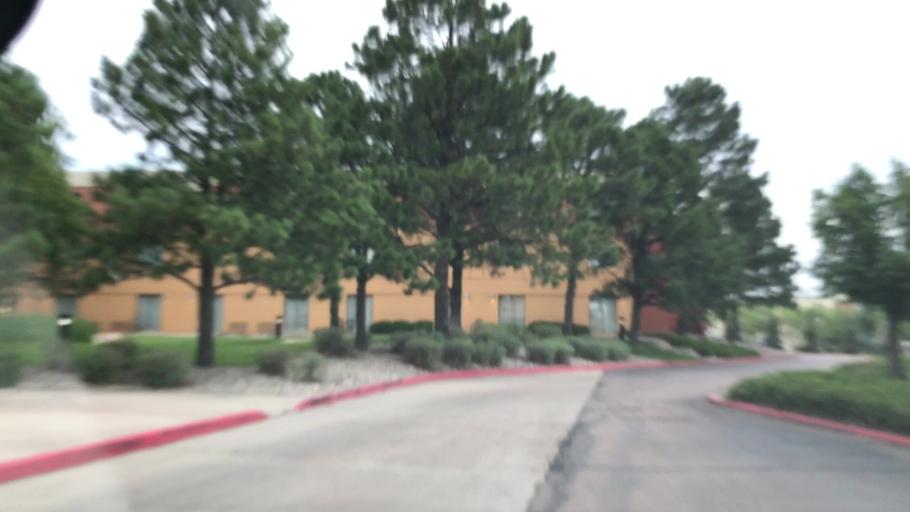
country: US
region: Colorado
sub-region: El Paso County
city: Stratmoor
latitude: 38.7990
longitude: -104.7954
